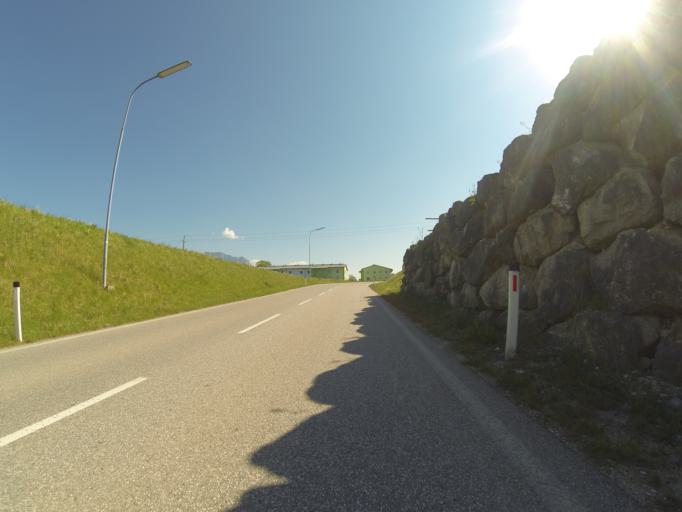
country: AT
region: Upper Austria
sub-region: Politischer Bezirk Gmunden
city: Gmunden
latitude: 47.9310
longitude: 13.7776
